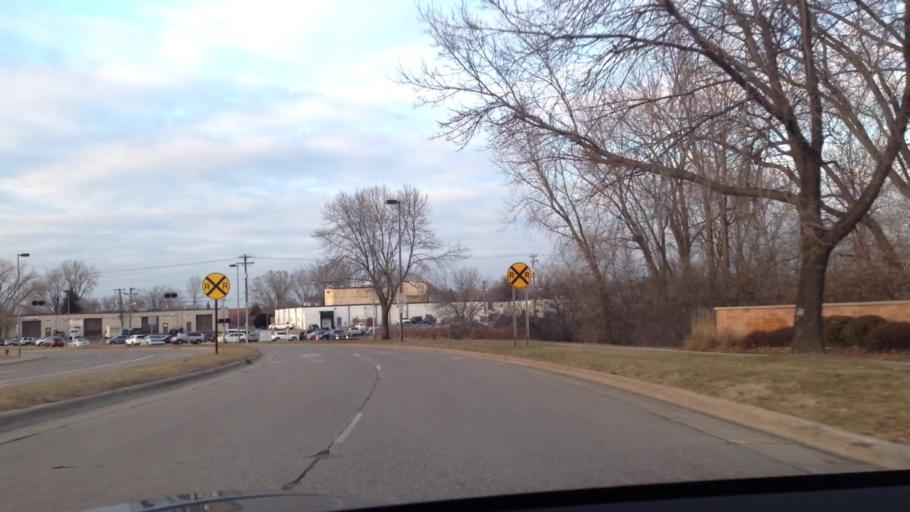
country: US
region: Minnesota
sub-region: Hennepin County
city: Saint Louis Park
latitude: 44.9314
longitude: -93.3652
